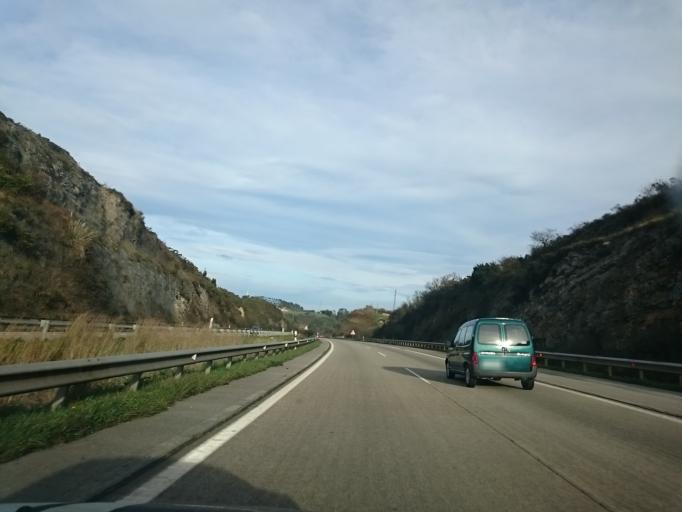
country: ES
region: Asturias
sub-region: Province of Asturias
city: Lugones
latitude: 43.4600
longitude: -5.7957
